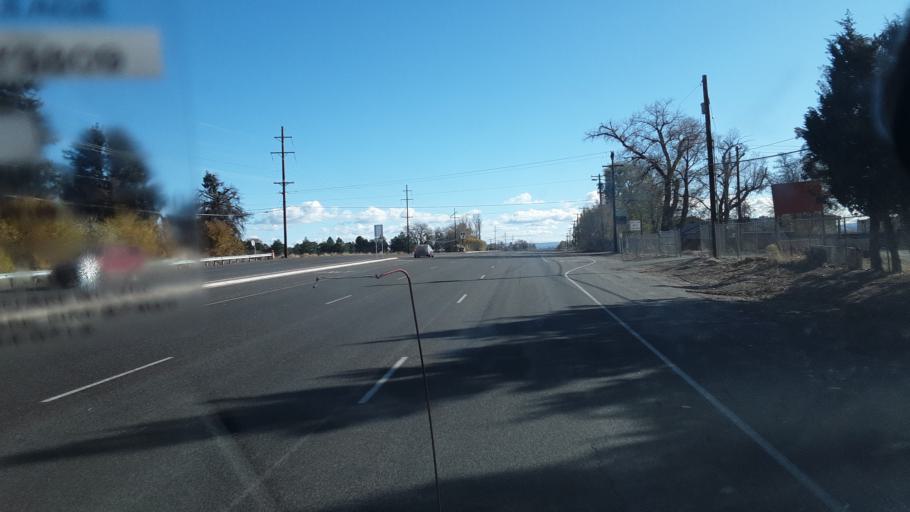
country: US
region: New Mexico
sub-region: San Juan County
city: Lee Acres
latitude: 36.7010
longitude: -108.0566
